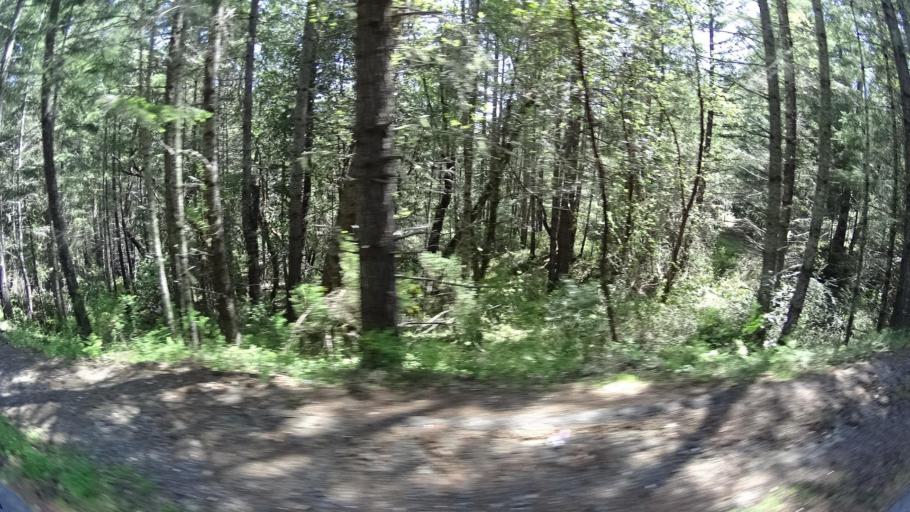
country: US
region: California
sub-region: Humboldt County
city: Redway
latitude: 40.1245
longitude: -123.6399
